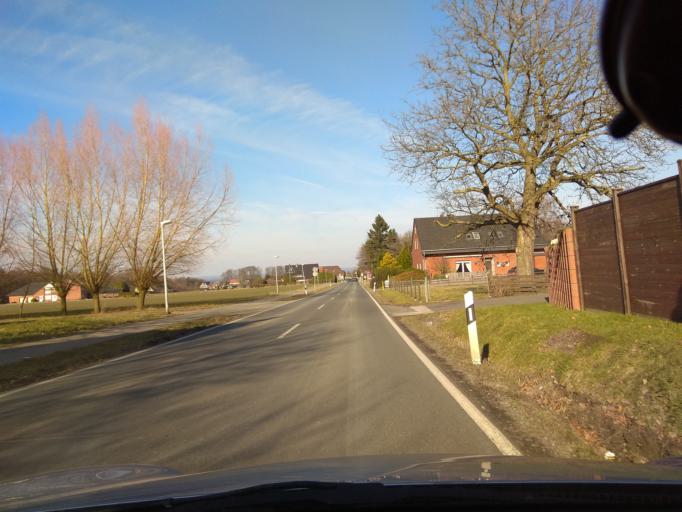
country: DE
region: North Rhine-Westphalia
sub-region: Regierungsbezirk Munster
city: Mettingen
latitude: 52.3016
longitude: 7.7767
